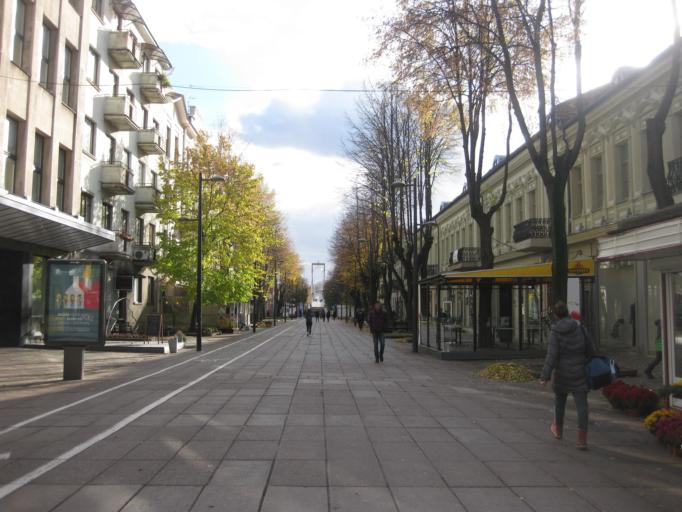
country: LT
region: Kauno apskritis
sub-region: Kaunas
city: Kaunas
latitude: 54.8961
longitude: 23.9134
